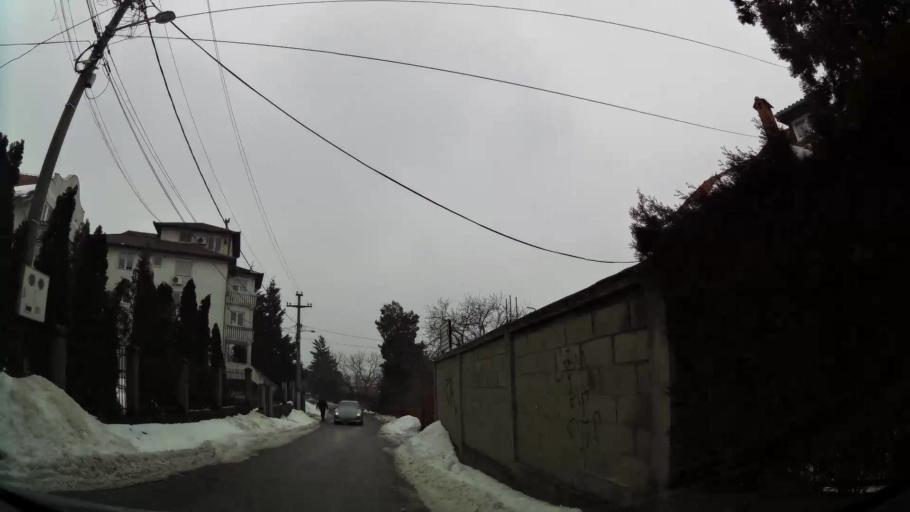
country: RS
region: Central Serbia
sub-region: Belgrade
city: Zvezdara
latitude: 44.7467
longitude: 20.5217
